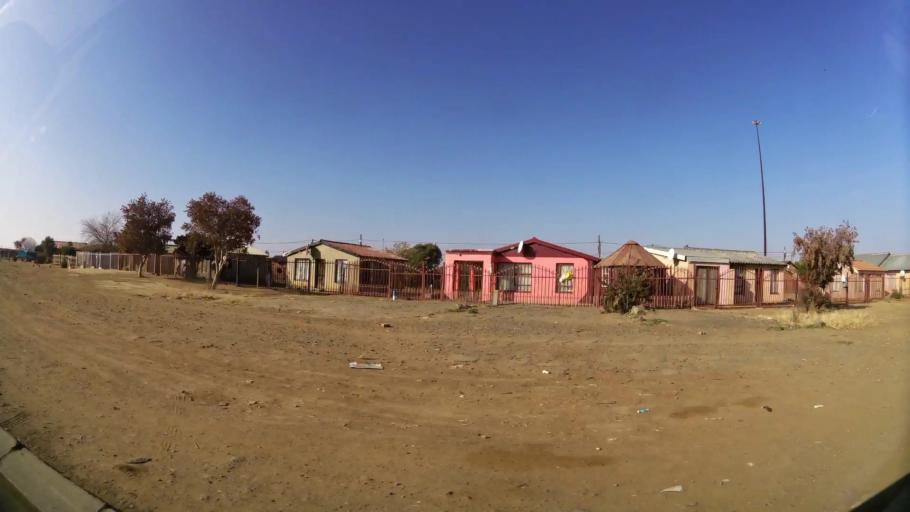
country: ZA
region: Orange Free State
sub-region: Mangaung Metropolitan Municipality
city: Bloemfontein
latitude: -29.1997
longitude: 26.2249
